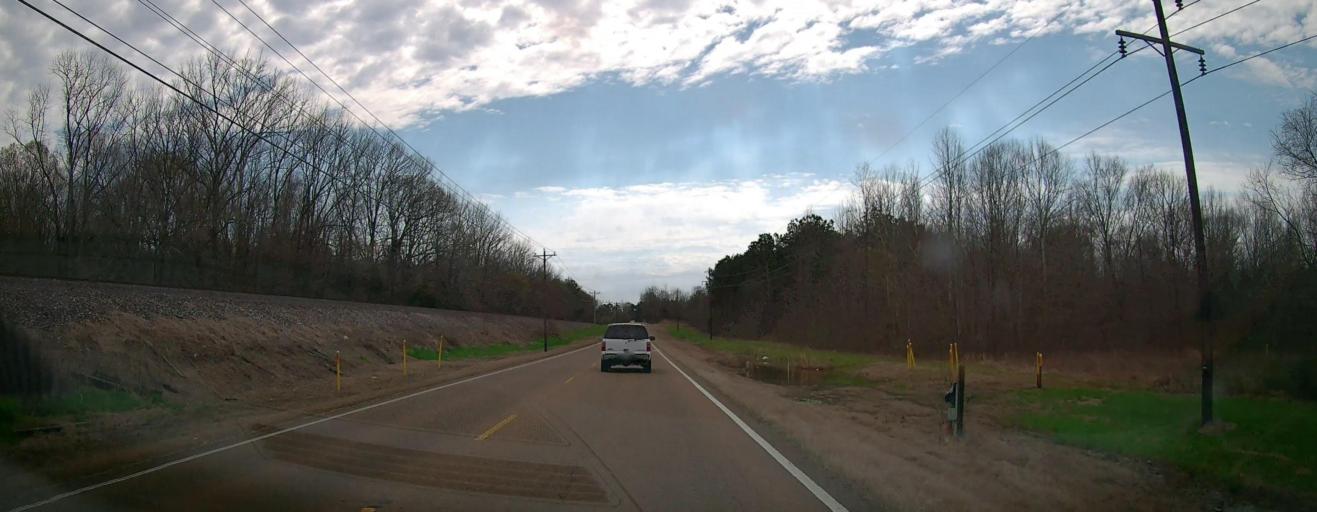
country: US
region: Mississippi
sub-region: Marshall County
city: Byhalia
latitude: 34.8939
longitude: -89.7361
